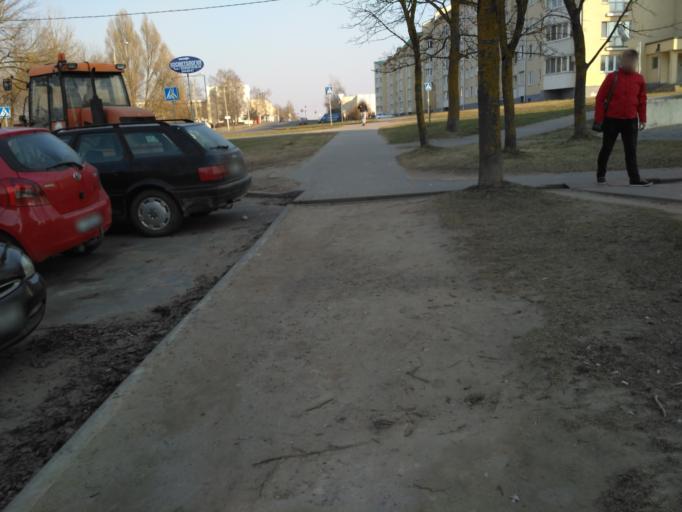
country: BY
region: Minsk
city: Zaslawye
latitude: 54.0131
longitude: 27.2610
